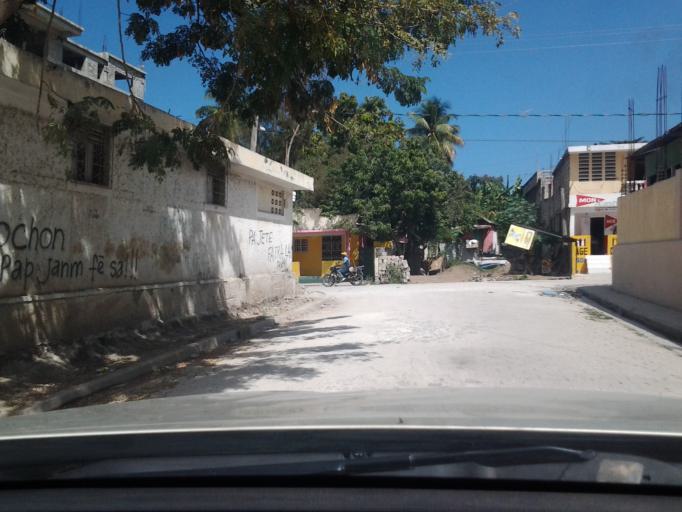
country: HT
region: Ouest
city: Tigwav
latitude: 18.4320
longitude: -72.8645
